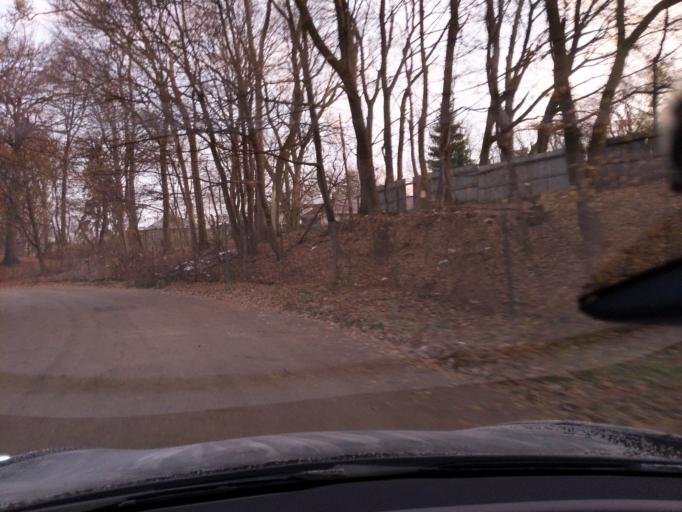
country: US
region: Michigan
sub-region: Ingham County
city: Lansing
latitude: 42.7087
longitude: -84.5530
